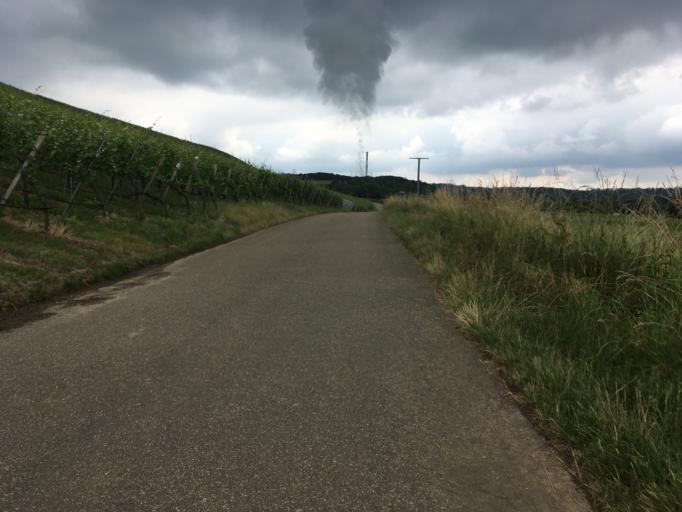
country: DE
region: Baden-Wuerttemberg
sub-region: Regierungsbezirk Stuttgart
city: Neckarwestheim
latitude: 49.0553
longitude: 9.1793
